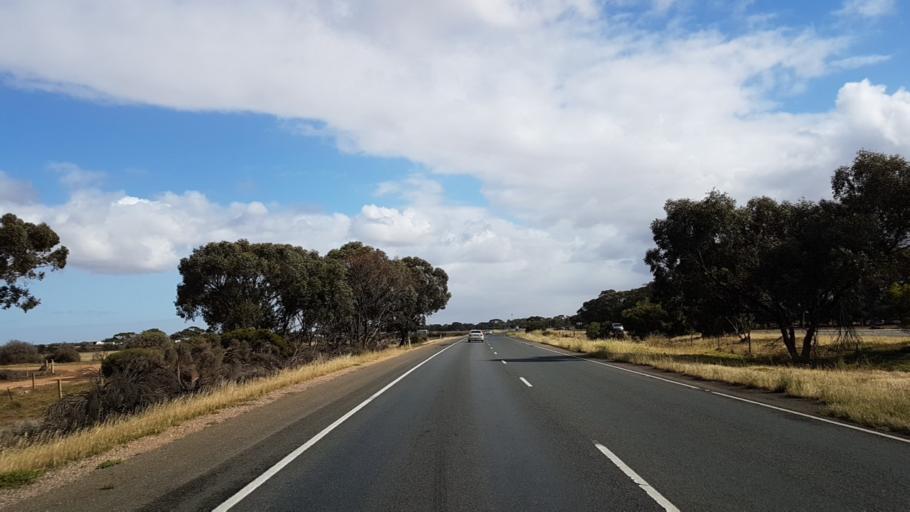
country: AU
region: South Australia
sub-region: Mallala
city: Two Wells
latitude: -34.6103
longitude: 138.5166
